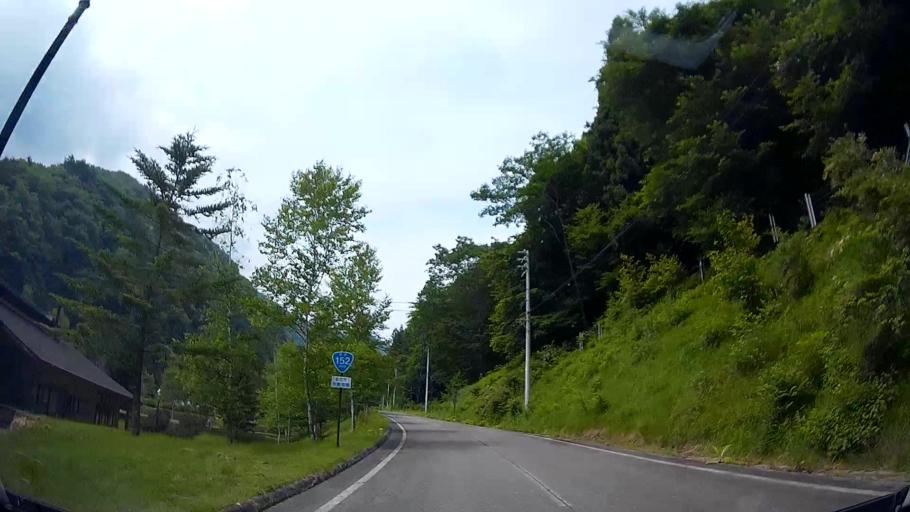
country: JP
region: Nagano
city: Iida
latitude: 35.4602
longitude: 137.9993
